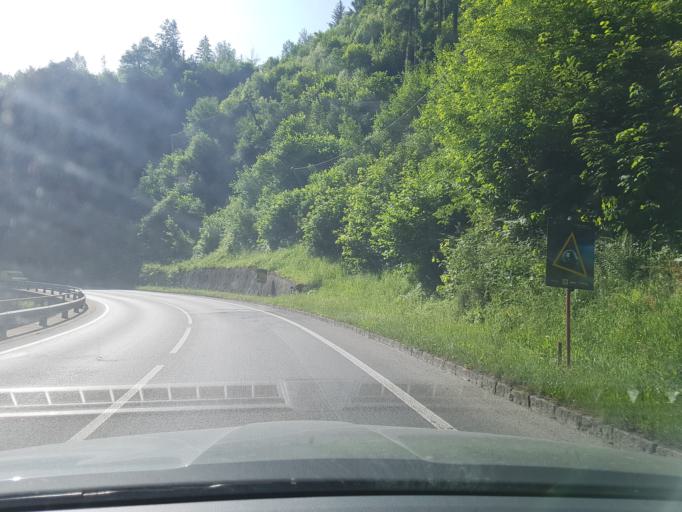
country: AT
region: Carinthia
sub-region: Politischer Bezirk Spittal an der Drau
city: Spittal an der Drau
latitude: 46.8099
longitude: 13.4921
